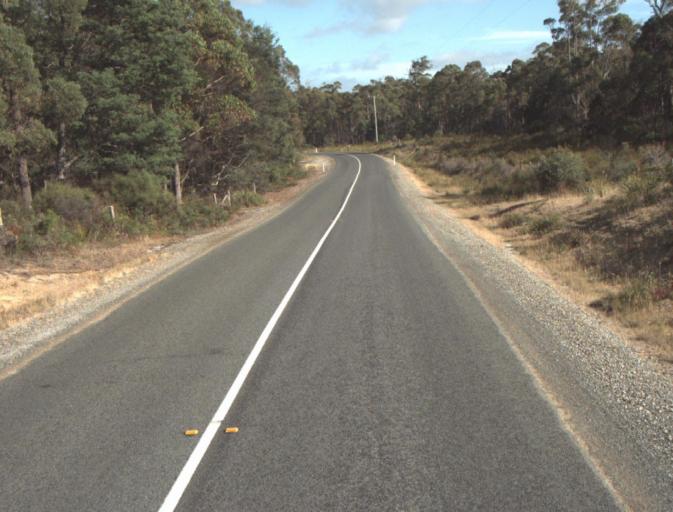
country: AU
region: Tasmania
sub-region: Dorset
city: Bridport
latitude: -41.1385
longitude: 147.2270
